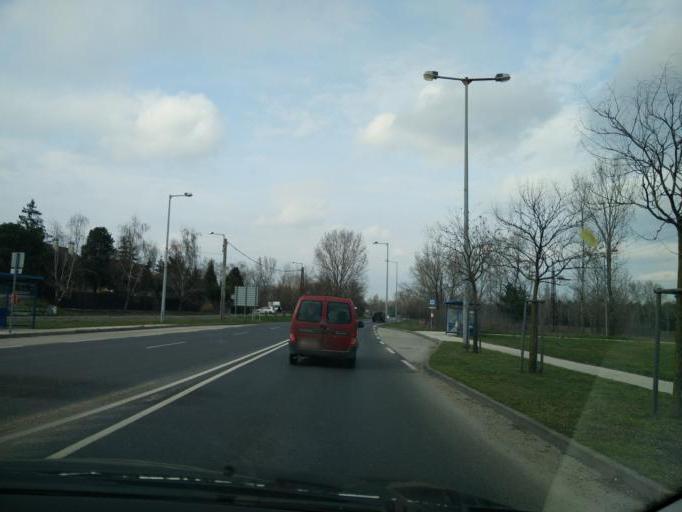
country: HU
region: Gyor-Moson-Sopron
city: Gyor
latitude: 47.7049
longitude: 17.6728
